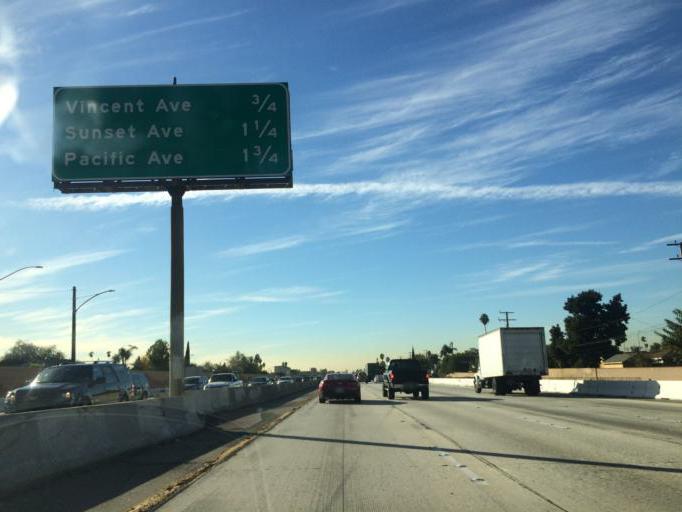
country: US
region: California
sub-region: Los Angeles County
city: Covina
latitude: 34.0722
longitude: -117.9114
